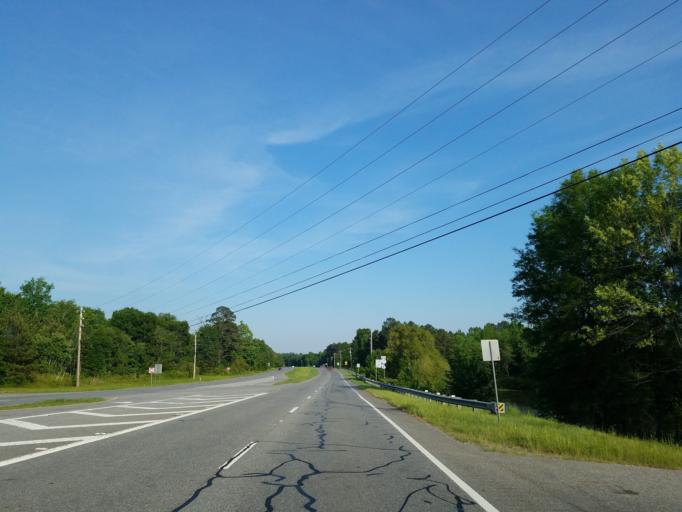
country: US
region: Georgia
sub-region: Chattooga County
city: Summerville
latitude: 34.4153
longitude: -85.2345
